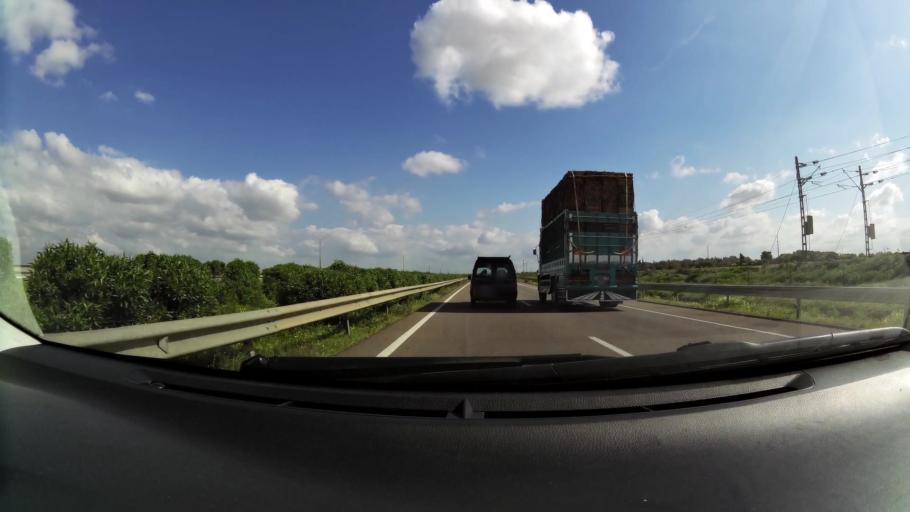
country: MA
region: Chaouia-Ouardigha
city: Nouaseur
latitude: 33.3451
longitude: -7.6139
